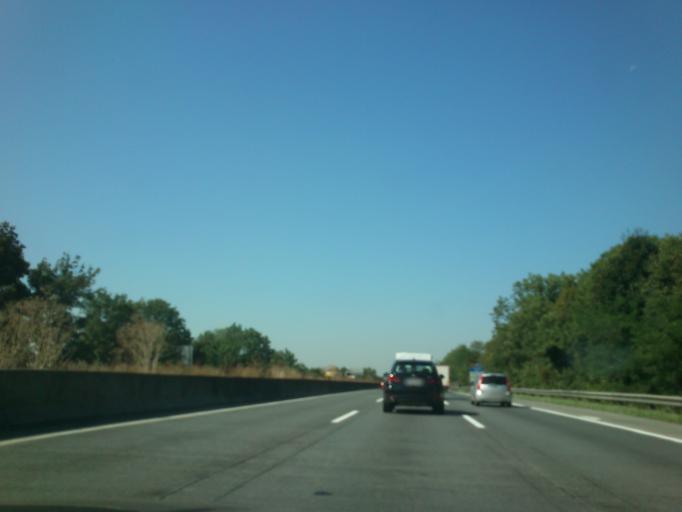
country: AT
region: Upper Austria
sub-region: Politischer Bezirk Linz-Land
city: Ansfelden
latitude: 48.2048
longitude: 14.2624
